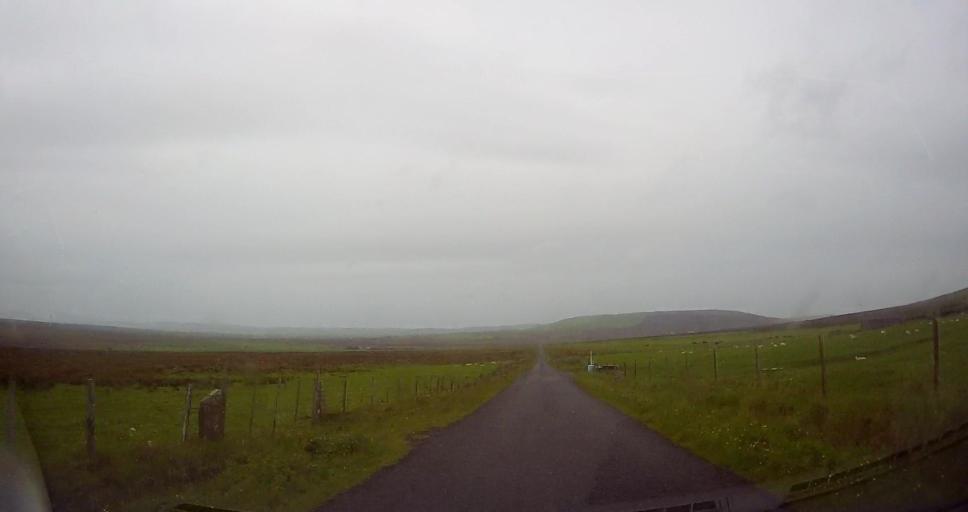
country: GB
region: Scotland
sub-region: Orkney Islands
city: Stromness
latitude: 59.0947
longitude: -3.1672
